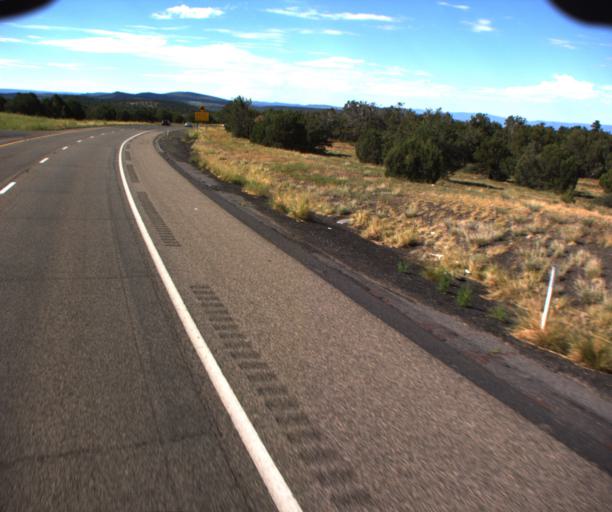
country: US
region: Arizona
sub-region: Yavapai County
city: Village of Oak Creek (Big Park)
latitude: 34.8049
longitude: -111.5982
